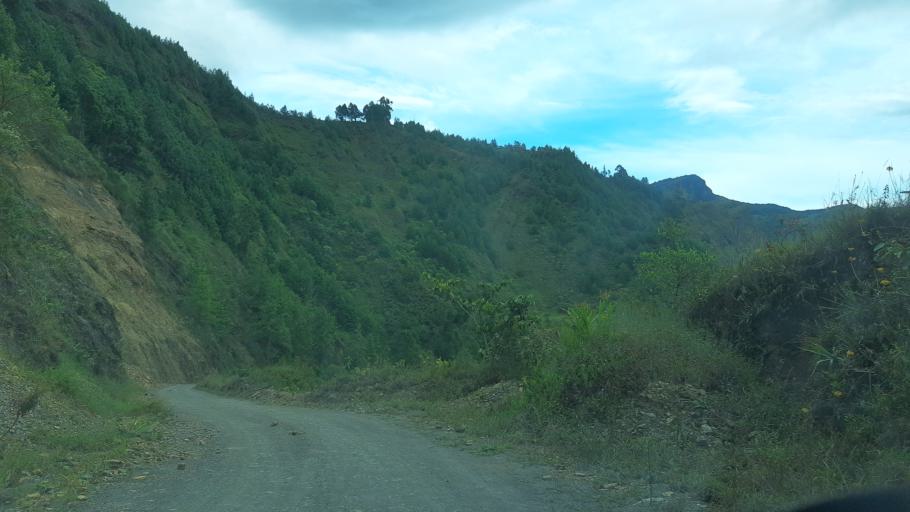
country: CO
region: Boyaca
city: Garagoa
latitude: 4.9995
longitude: -73.3360
